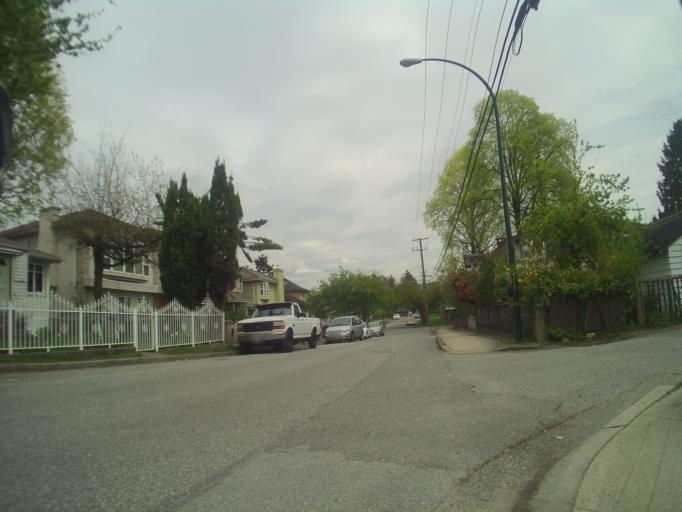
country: CA
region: British Columbia
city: Vancouver
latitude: 49.2430
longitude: -123.0730
